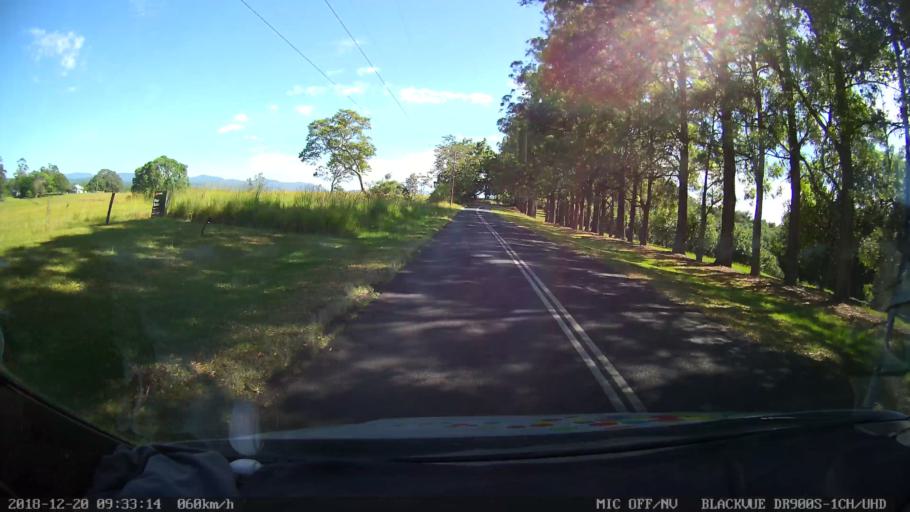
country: AU
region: New South Wales
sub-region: Lismore Municipality
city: Goonellabah
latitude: -28.6969
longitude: 153.3075
